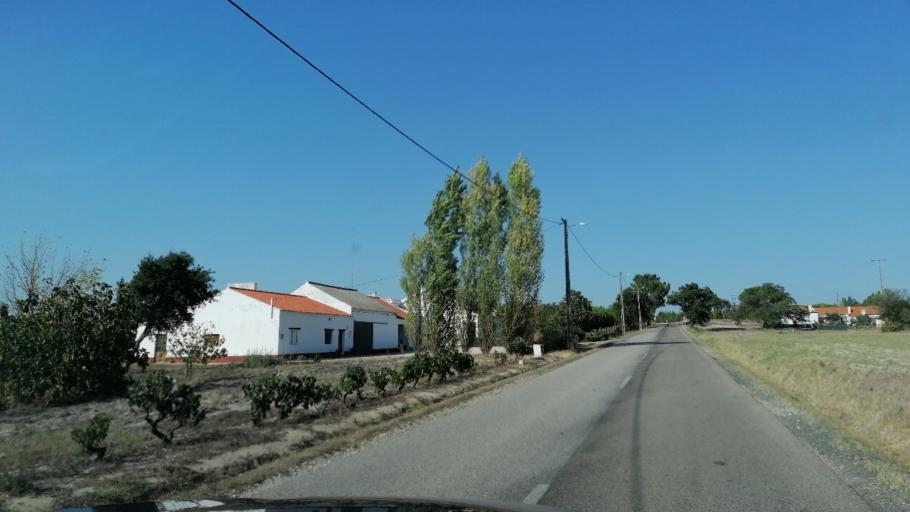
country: PT
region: Santarem
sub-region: Coruche
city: Coruche
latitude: 38.8191
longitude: -8.5700
